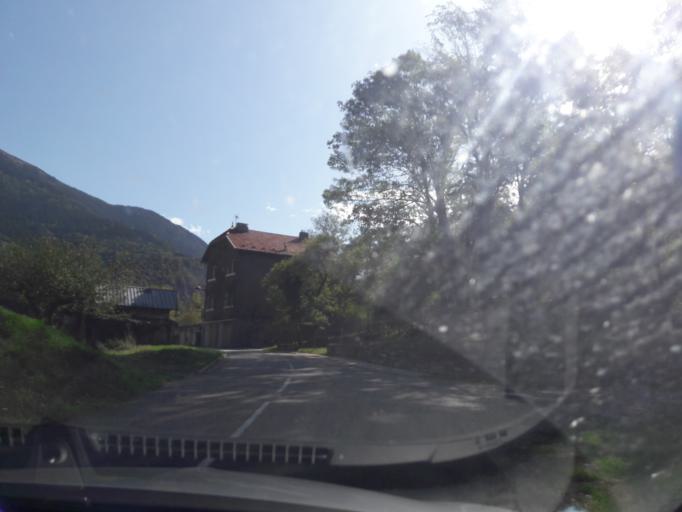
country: FR
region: Rhone-Alpes
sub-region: Departement de la Savoie
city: Saint-Jean-de-Maurienne
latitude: 45.3085
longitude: 6.3559
